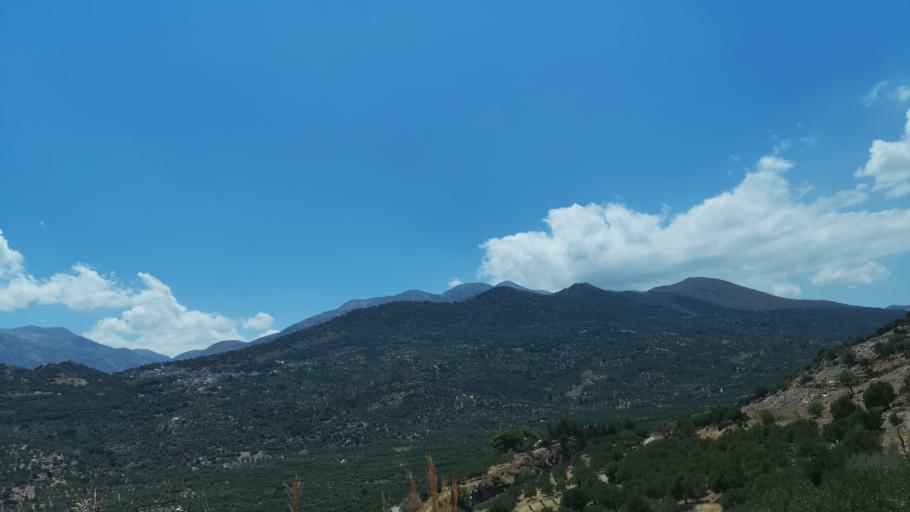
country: GR
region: Crete
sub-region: Nomos Lasithiou
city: Neapoli
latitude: 35.2511
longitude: 25.6316
